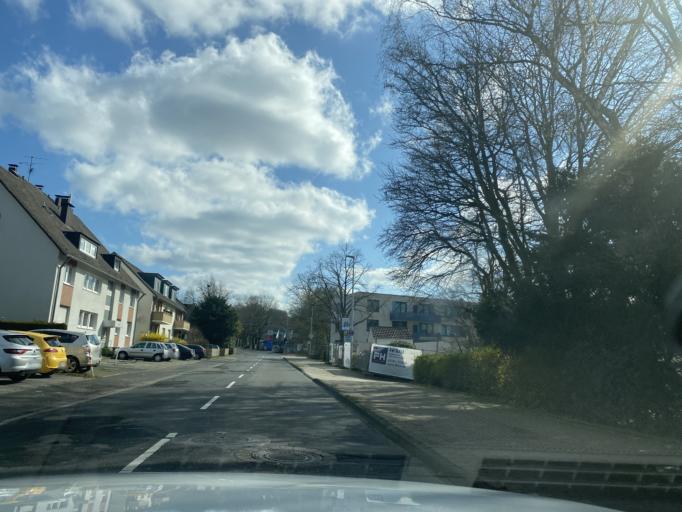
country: DE
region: North Rhine-Westphalia
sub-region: Regierungsbezirk Koln
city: Bergisch Gladbach
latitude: 50.9798
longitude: 7.1402
